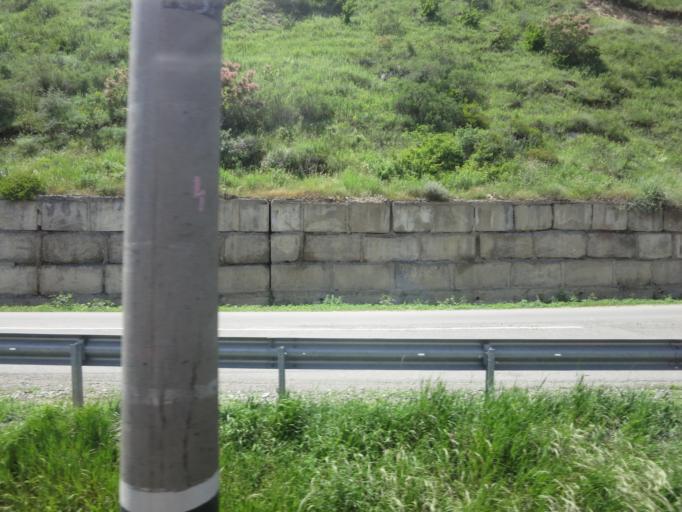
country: GE
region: Shida Kartli
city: Gori
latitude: 41.9787
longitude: 44.0857
